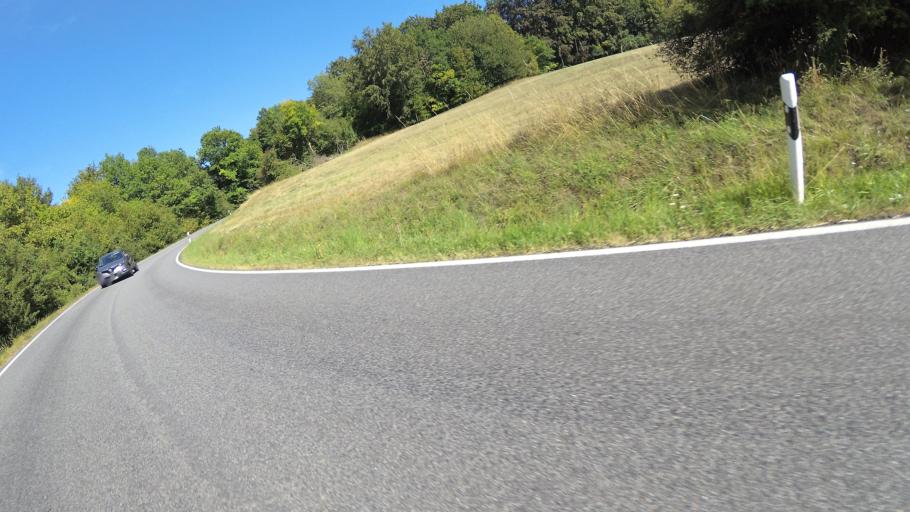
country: DE
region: Saarland
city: Gersheim
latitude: 49.1591
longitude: 7.2518
